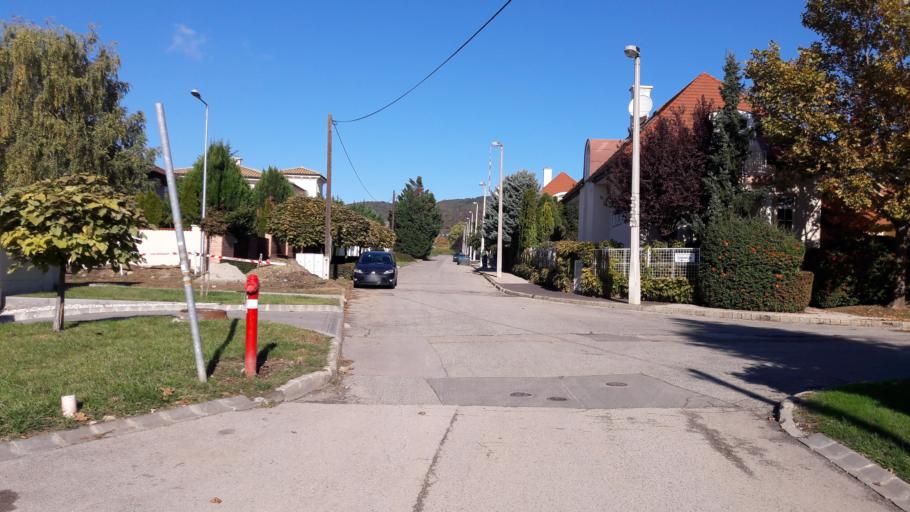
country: HU
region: Pest
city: Budaors
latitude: 47.4704
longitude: 18.9869
